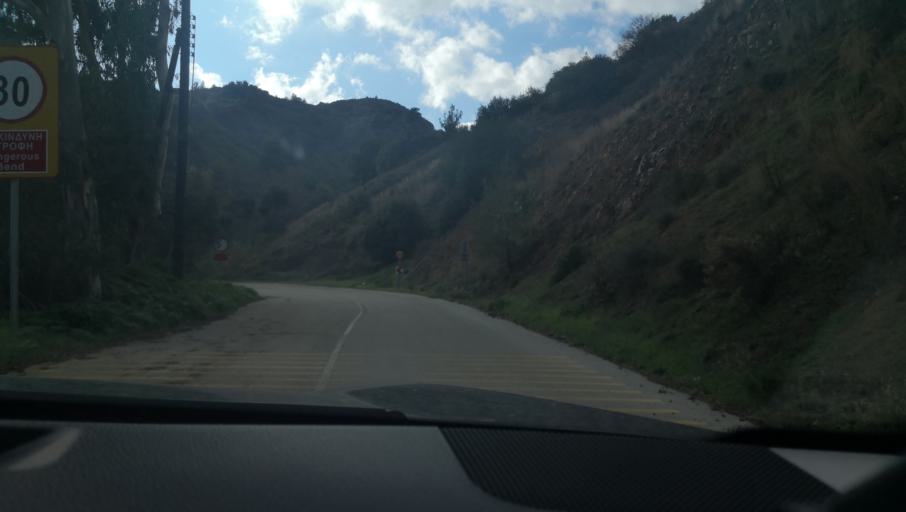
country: CY
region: Lefkosia
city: Lefka
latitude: 35.0443
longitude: 32.7337
